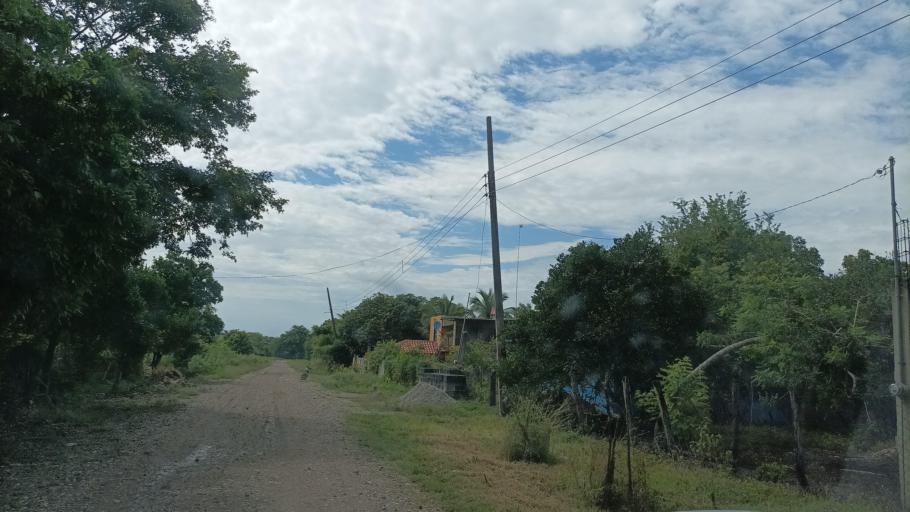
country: MX
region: Veracruz
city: Panuco
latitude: 21.9435
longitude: -98.1373
